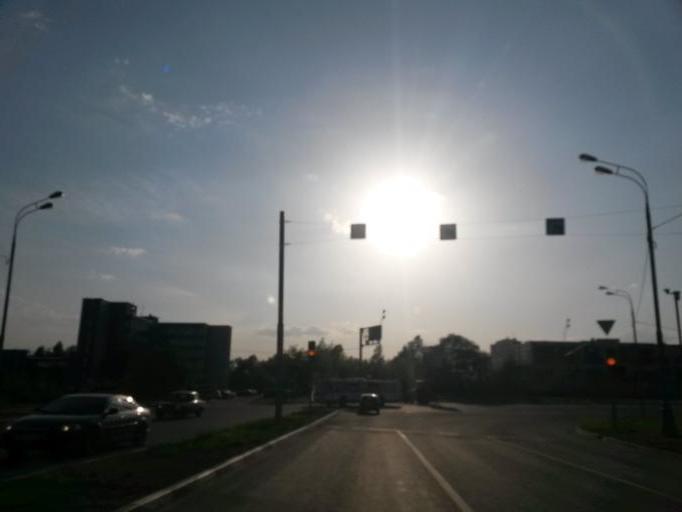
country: RU
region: Moskovskaya
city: Biryulevo Zapadnoye
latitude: 55.5880
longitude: 37.6361
